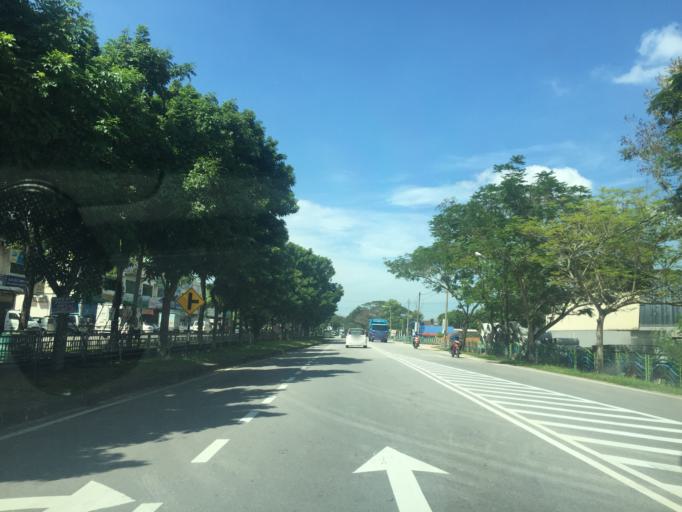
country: MY
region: Penang
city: Tasek Glugor
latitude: 5.4849
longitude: 100.4856
